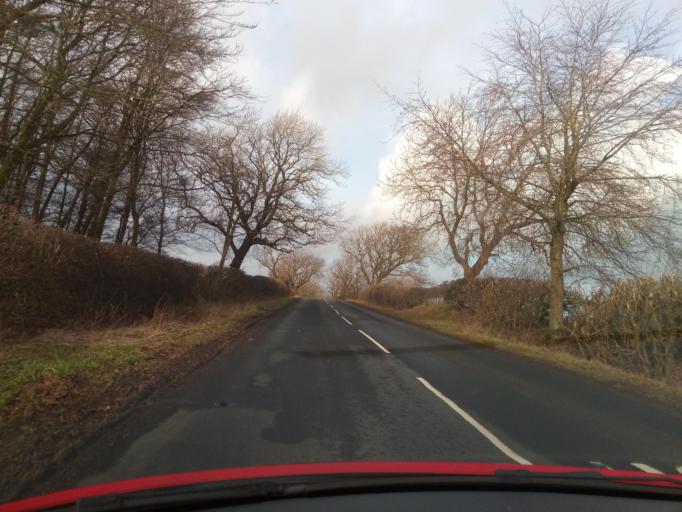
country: GB
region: England
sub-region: Northumberland
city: Rothley
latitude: 55.1110
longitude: -2.0088
